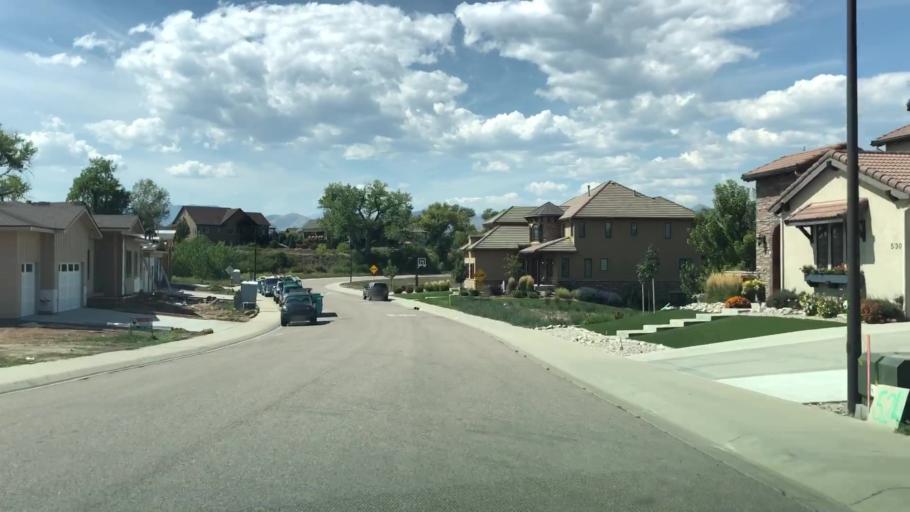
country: US
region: Colorado
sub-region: Larimer County
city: Loveland
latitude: 40.3965
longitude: -105.1499
